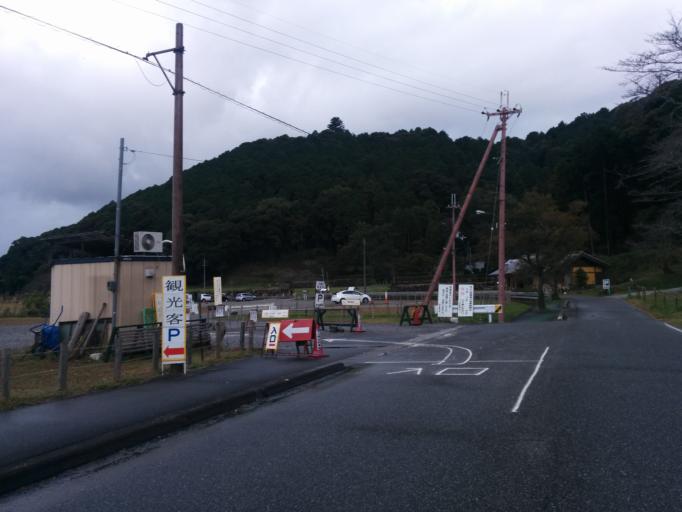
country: JP
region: Shiga Prefecture
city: Omihachiman
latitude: 35.1520
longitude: 136.1401
